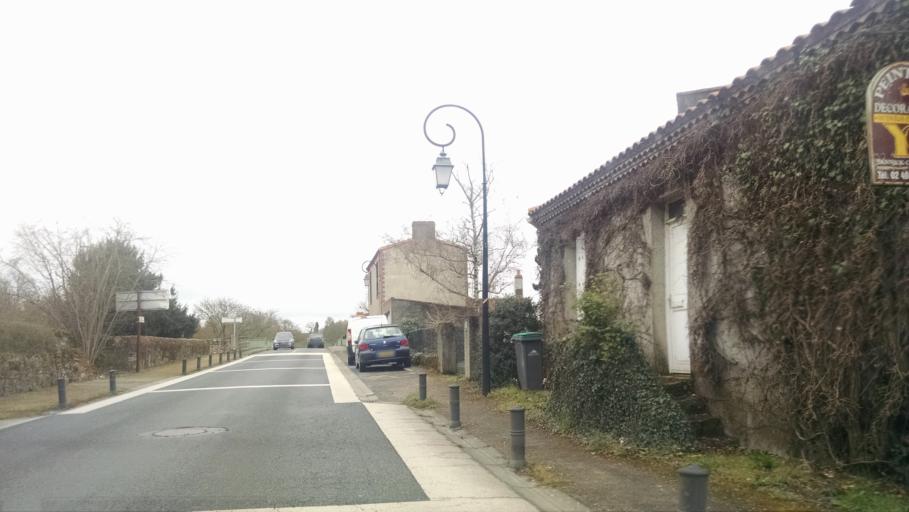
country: FR
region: Pays de la Loire
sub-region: Departement de la Loire-Atlantique
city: Monnieres
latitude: 47.1369
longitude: -1.3536
